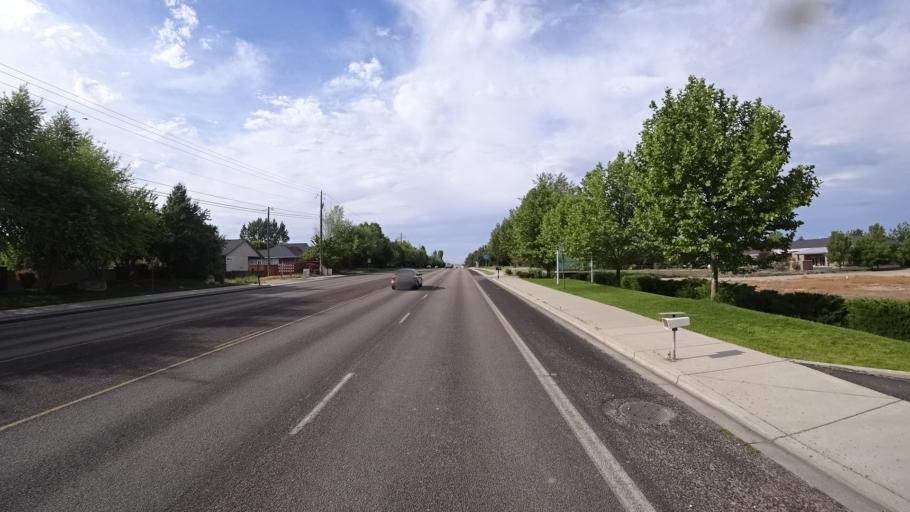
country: US
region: Idaho
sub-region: Ada County
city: Meridian
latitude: 43.6017
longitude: -116.3746
